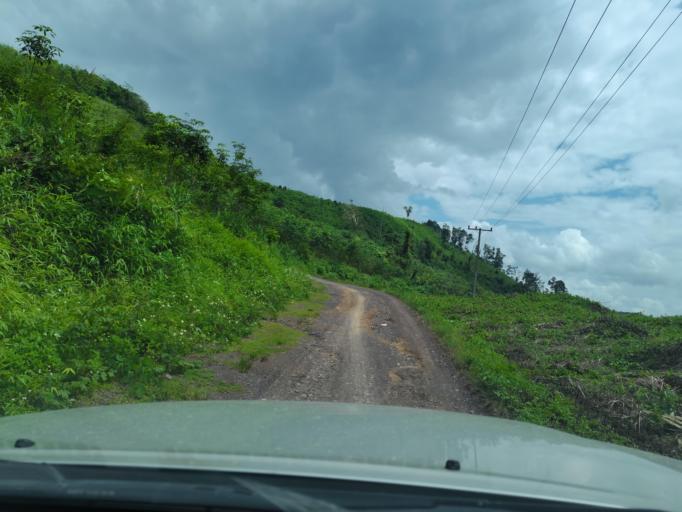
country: LA
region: Loungnamtha
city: Muang Long
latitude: 20.7154
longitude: 101.0140
